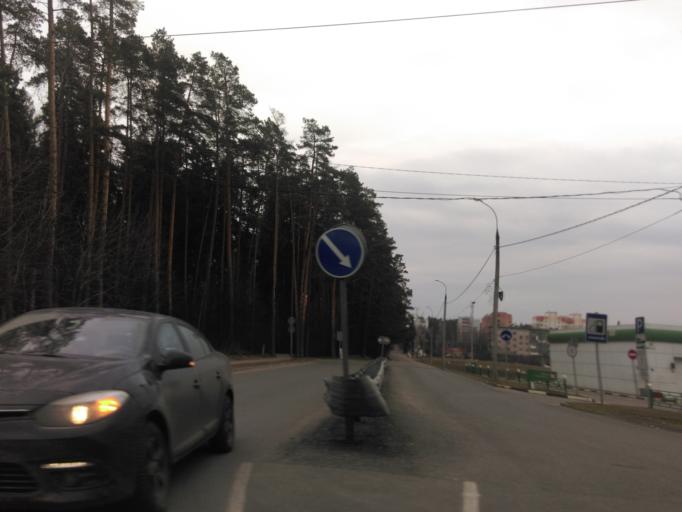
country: RU
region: Moskovskaya
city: Petrovo-Dal'neye
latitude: 55.7345
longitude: 37.2244
